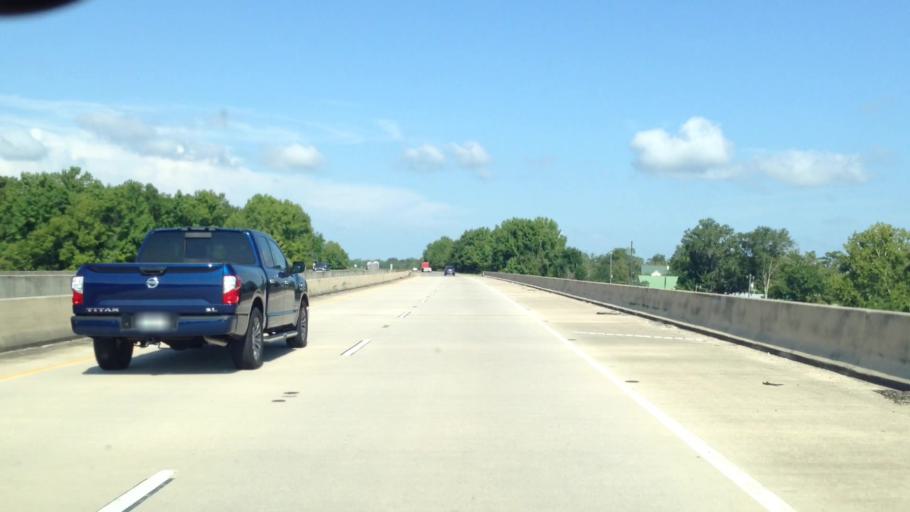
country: US
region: Louisiana
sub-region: Saint Landry Parish
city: Krotz Springs
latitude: 30.5485
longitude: -91.8312
